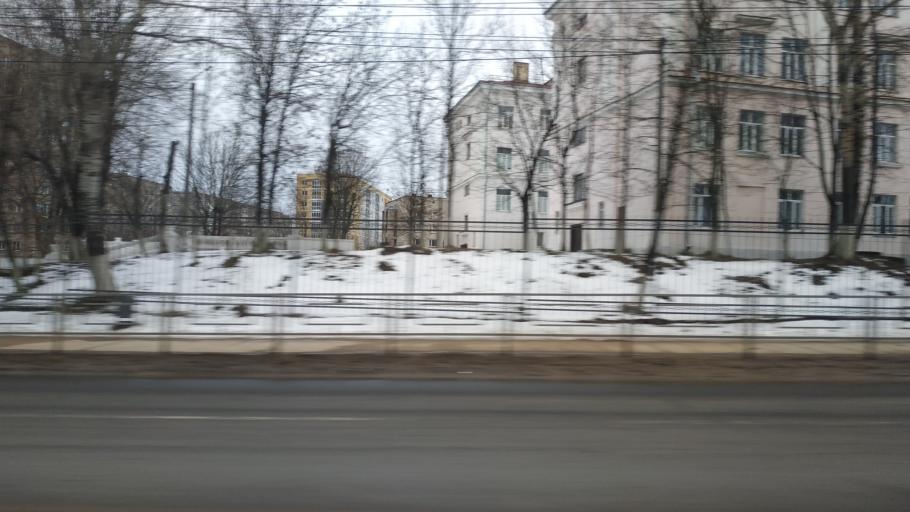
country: RU
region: Tverskaya
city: Tver
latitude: 56.8516
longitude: 35.9248
